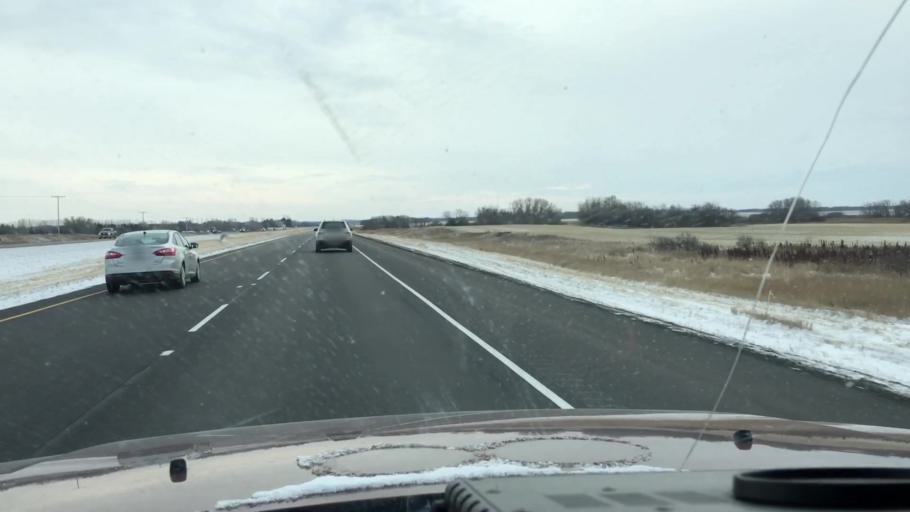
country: CA
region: Saskatchewan
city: Saskatoon
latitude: 52.0254
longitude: -106.5811
